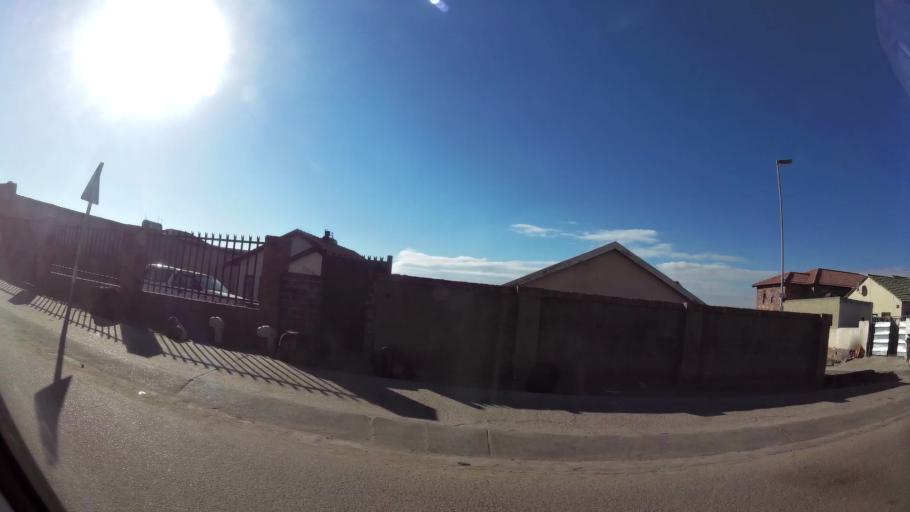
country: ZA
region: Gauteng
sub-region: City of Johannesburg Metropolitan Municipality
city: Midrand
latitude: -25.9076
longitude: 28.0990
